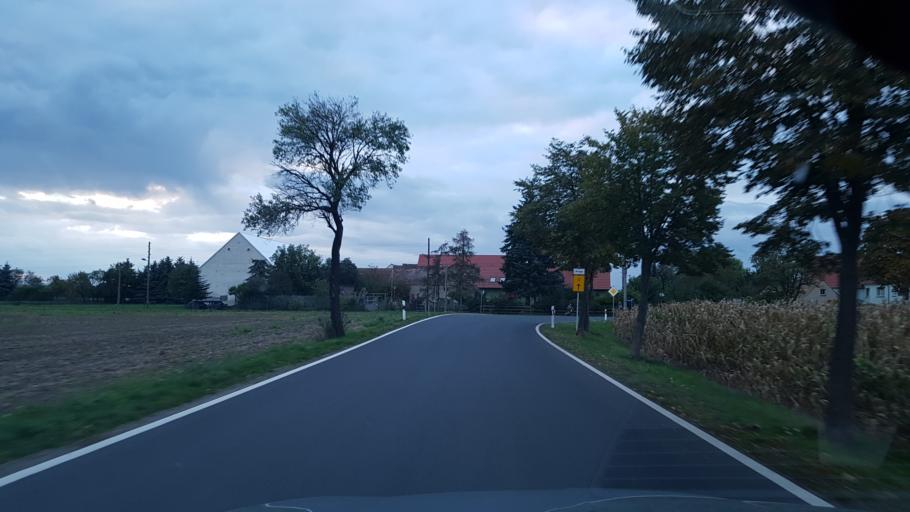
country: DE
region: Saxony
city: Grossenhain
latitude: 51.3251
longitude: 13.5603
